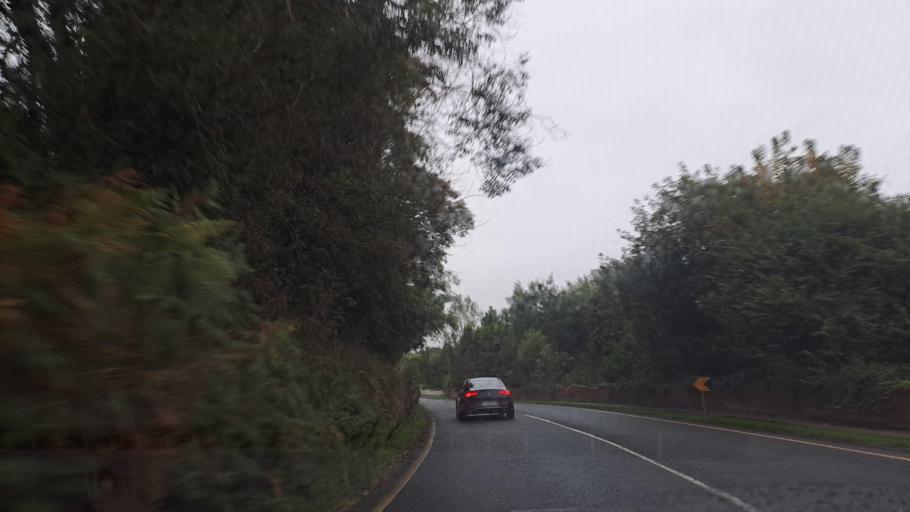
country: IE
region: Ulster
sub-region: County Monaghan
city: Monaghan
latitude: 54.2296
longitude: -6.9568
